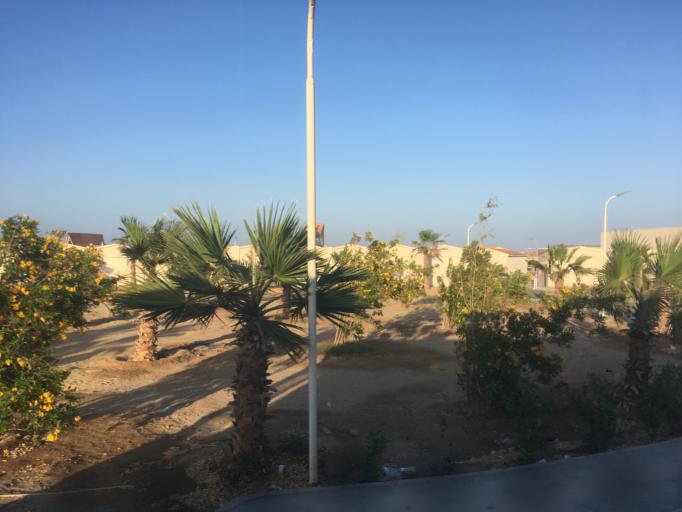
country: EG
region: Red Sea
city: Al Qusayr
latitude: 25.9640
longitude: 34.3599
